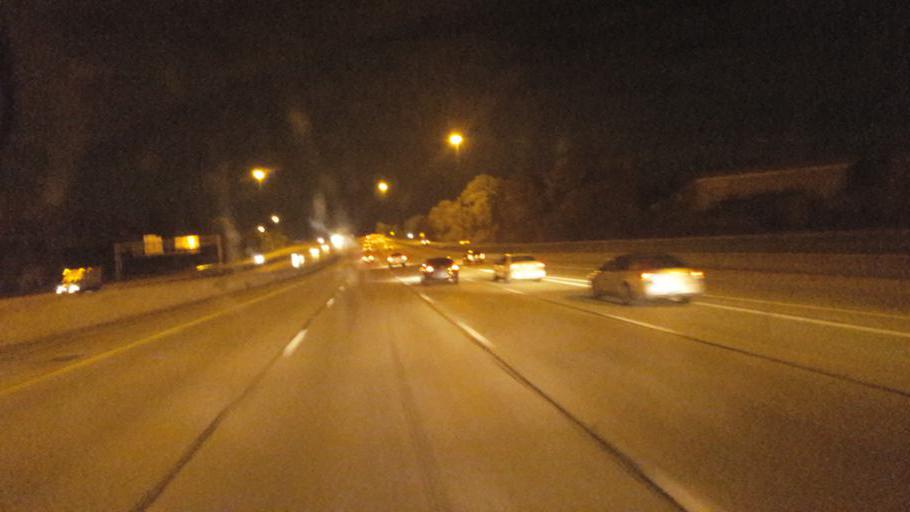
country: US
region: Indiana
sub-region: Marion County
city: Warren Park
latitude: 39.8003
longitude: -86.0491
